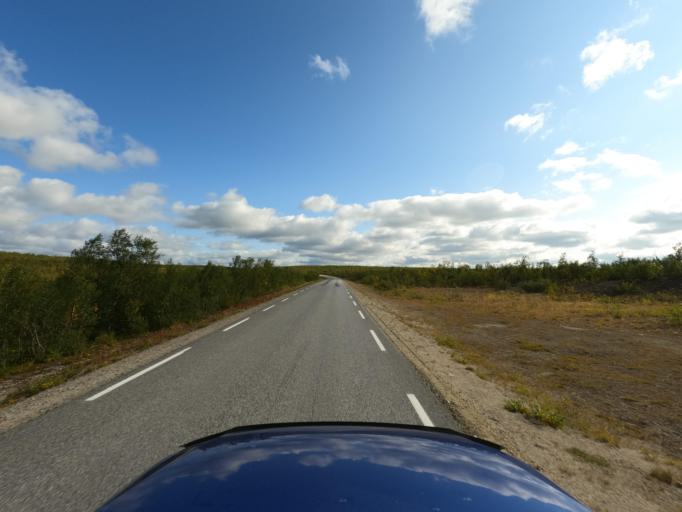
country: NO
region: Finnmark Fylke
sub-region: Porsanger
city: Lakselv
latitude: 69.3911
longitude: 24.5341
